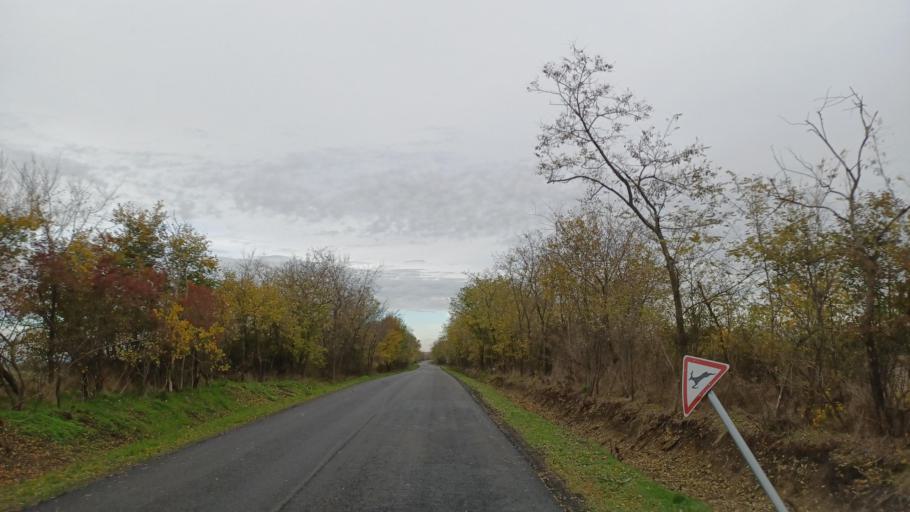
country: HU
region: Tolna
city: Tengelic
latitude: 46.5410
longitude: 18.7565
